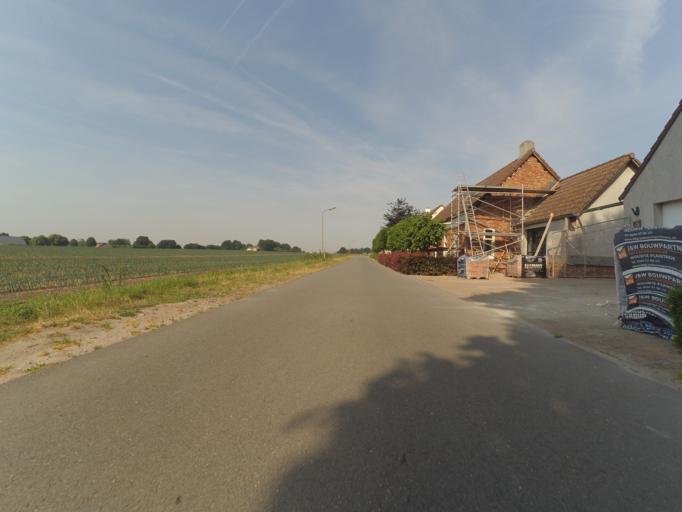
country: NL
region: North Brabant
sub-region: Gemeente Woensdrecht
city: Woensdrecht
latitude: 51.3873
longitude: 4.3445
